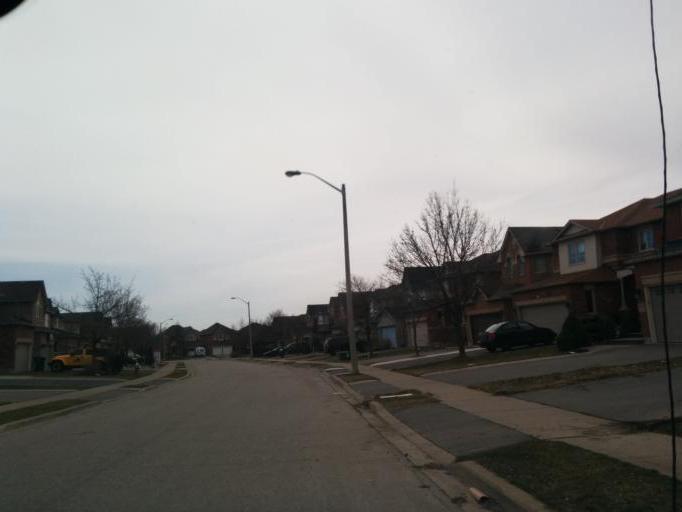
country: CA
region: Ontario
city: Brampton
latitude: 43.7299
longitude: -79.8239
